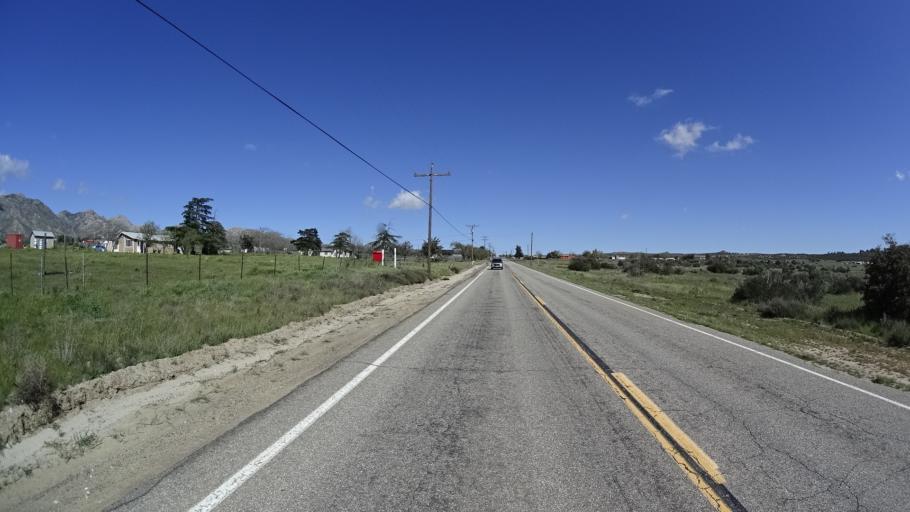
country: US
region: California
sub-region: San Diego County
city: Julian
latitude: 33.2103
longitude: -116.5289
